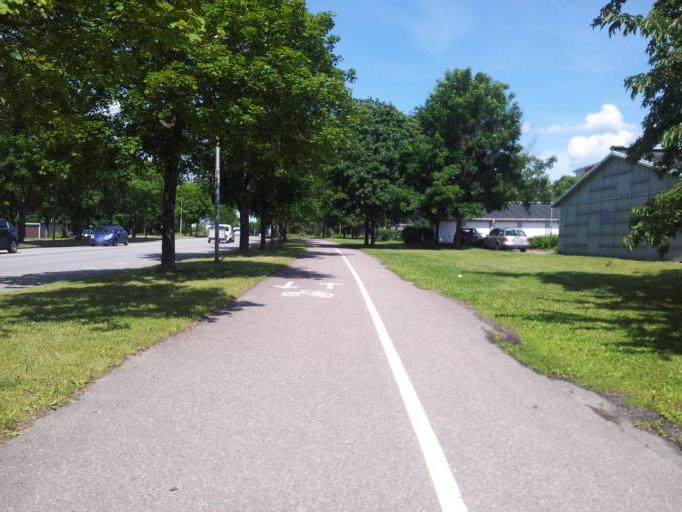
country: SE
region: Uppsala
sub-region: Uppsala Kommun
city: Uppsala
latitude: 59.8774
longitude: 17.6559
